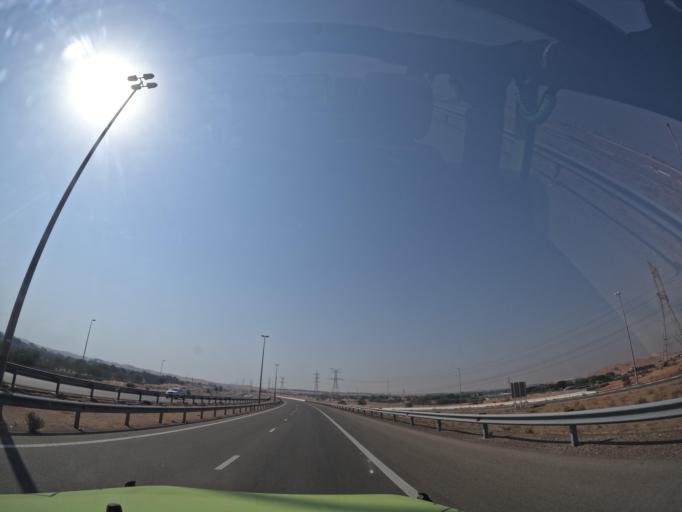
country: OM
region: Al Buraimi
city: Al Buraymi
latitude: 24.3682
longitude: 55.7284
